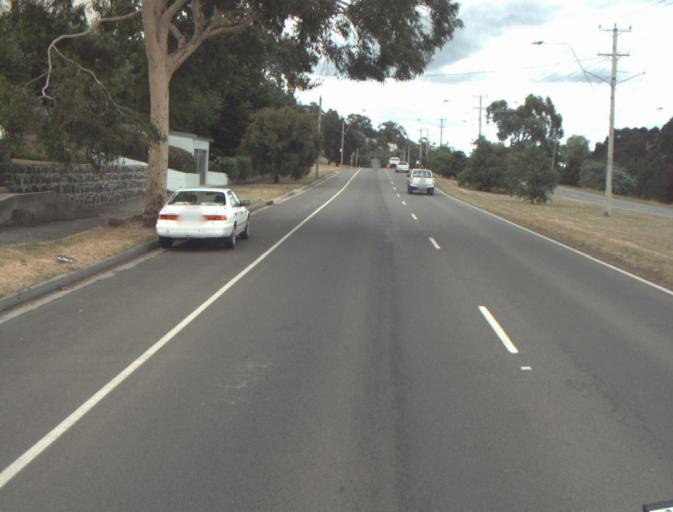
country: AU
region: Tasmania
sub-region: Launceston
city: Launceston
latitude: -41.4353
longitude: 147.1243
